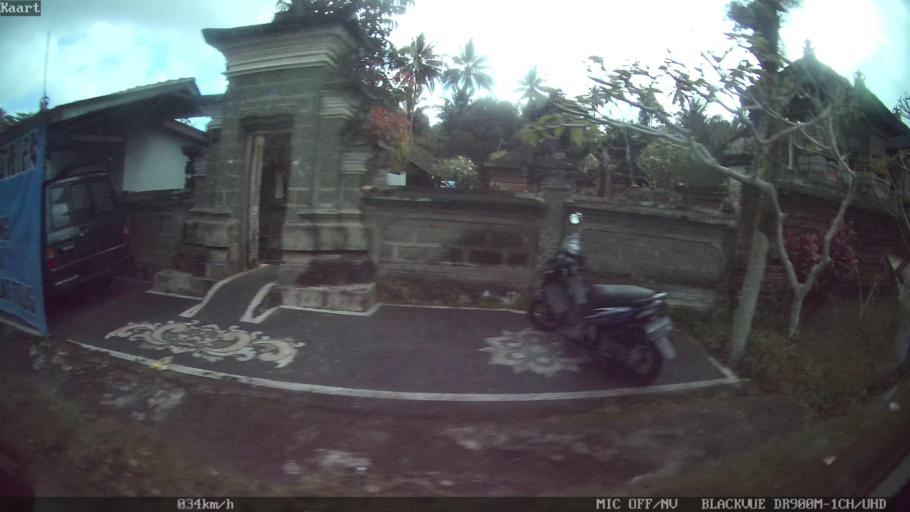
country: ID
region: Bali
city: Banjar Pesalakan
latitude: -8.4954
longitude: 115.3048
